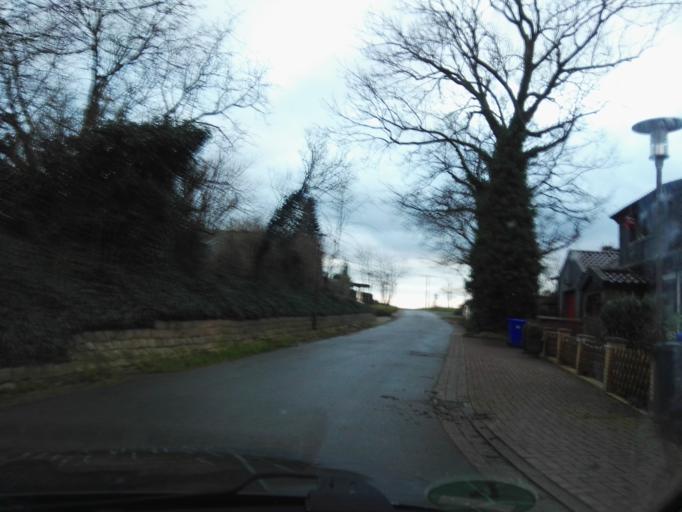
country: DE
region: Lower Saxony
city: Leiferde
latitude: 52.2077
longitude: 10.4667
